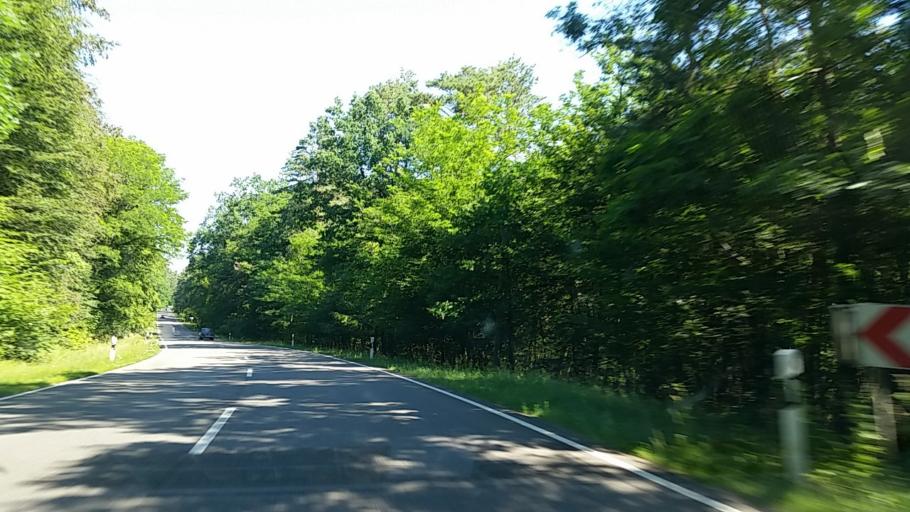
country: DE
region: Saxony
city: Bad Duben
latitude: 51.6638
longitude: 12.5999
